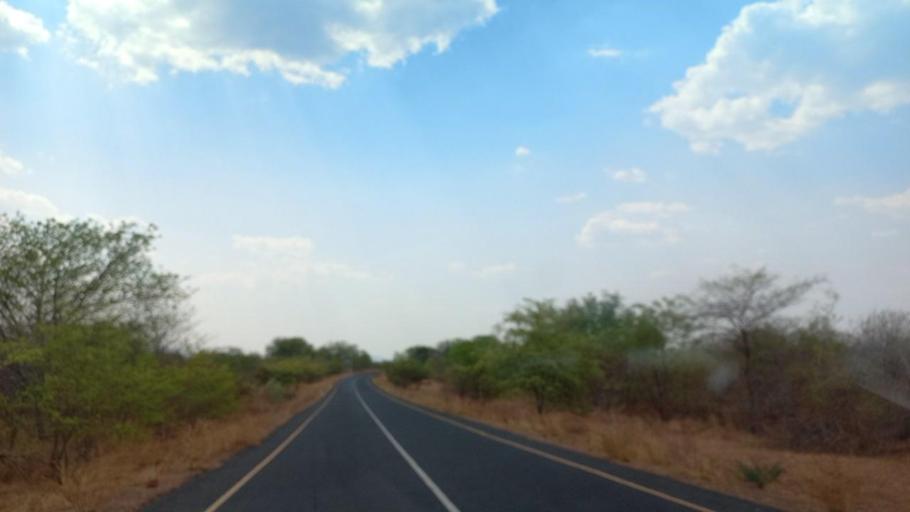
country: ZM
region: Lusaka
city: Luangwa
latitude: -15.2151
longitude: 30.2313
